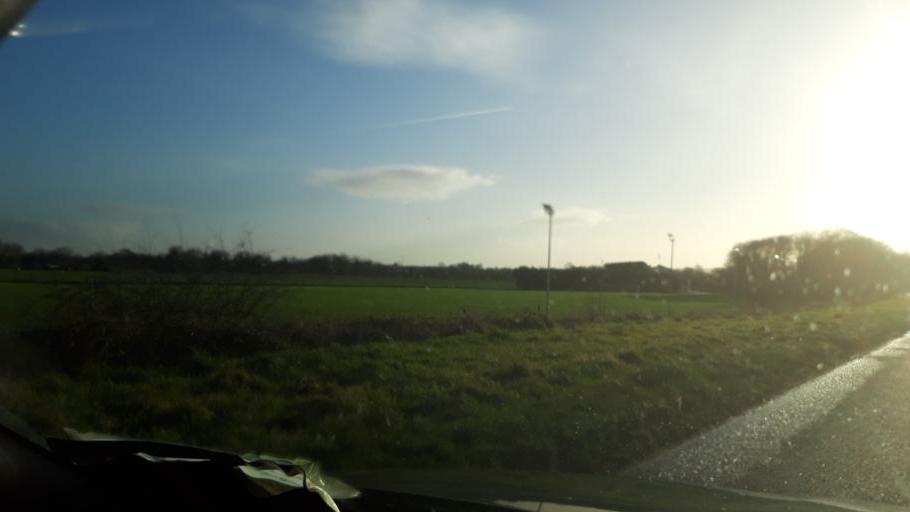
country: GB
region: Northern Ireland
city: Maghera
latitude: 54.8191
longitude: -6.6983
